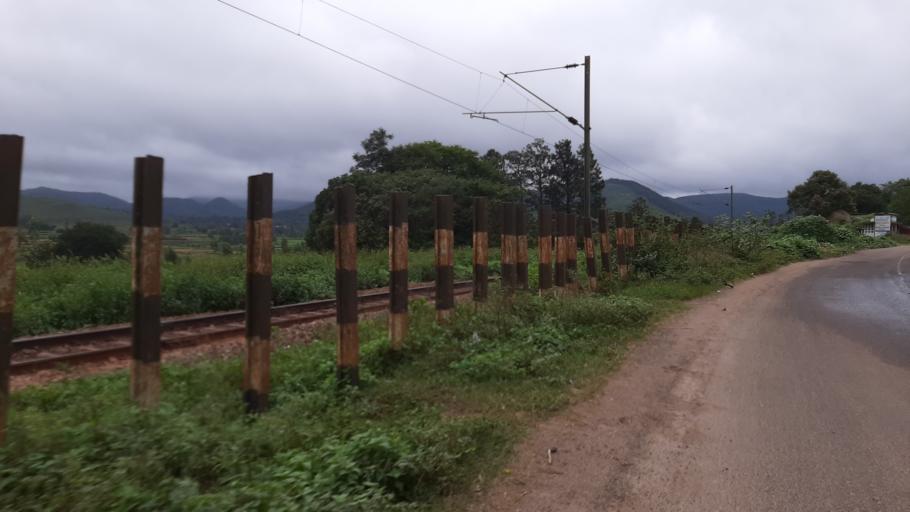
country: IN
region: Andhra Pradesh
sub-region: Vizianagaram District
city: Salur
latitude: 18.3051
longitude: 82.9053
